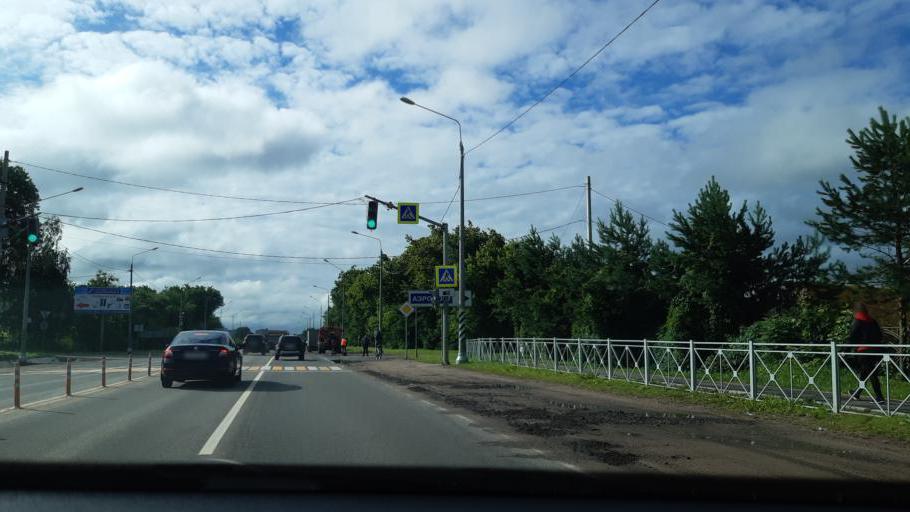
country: RU
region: Smolensk
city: Smolensk
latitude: 54.7529
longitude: 32.0747
